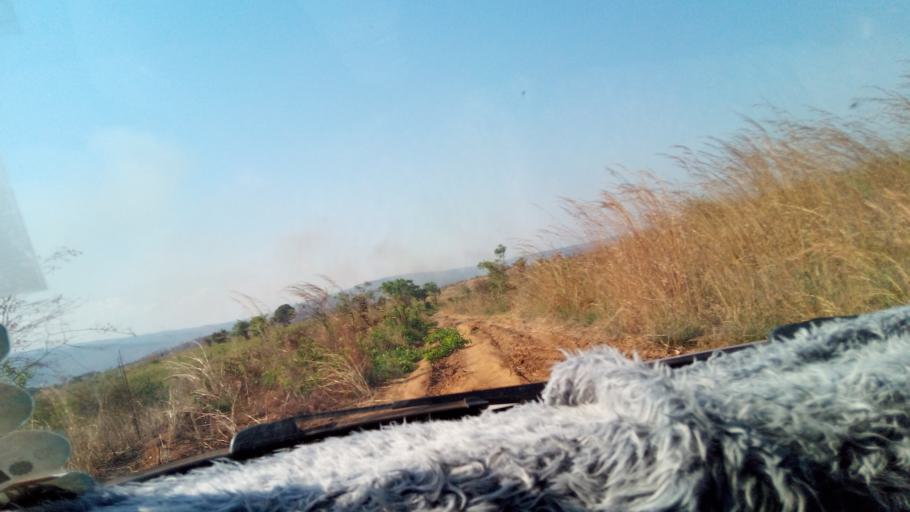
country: CD
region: Katanga
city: Kalemie
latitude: -5.9141
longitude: 29.1239
